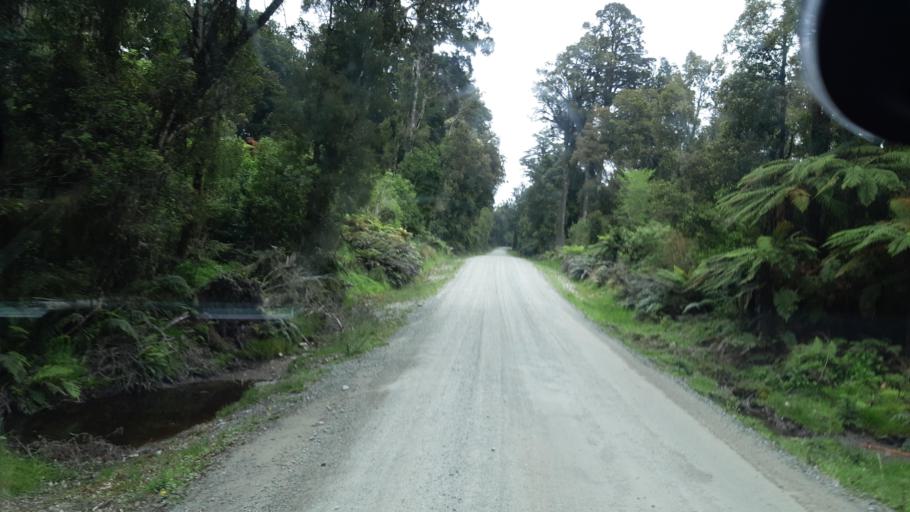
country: NZ
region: West Coast
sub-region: Grey District
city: Greymouth
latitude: -42.6457
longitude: 171.3451
